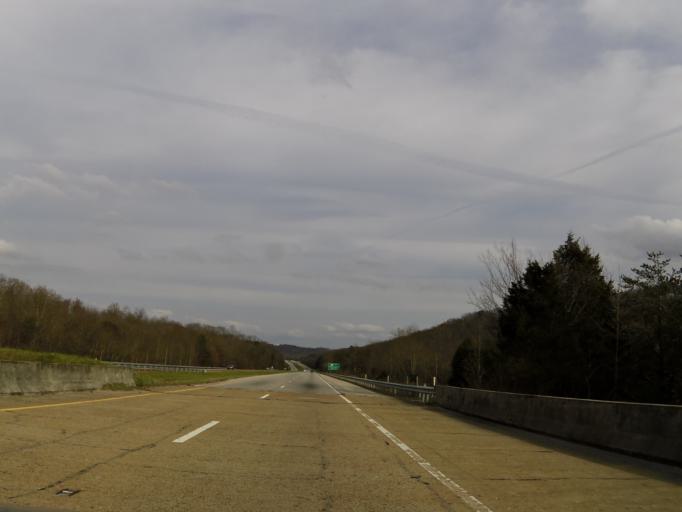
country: US
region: Tennessee
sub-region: Hamilton County
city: Falling Water
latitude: 35.1796
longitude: -85.2682
